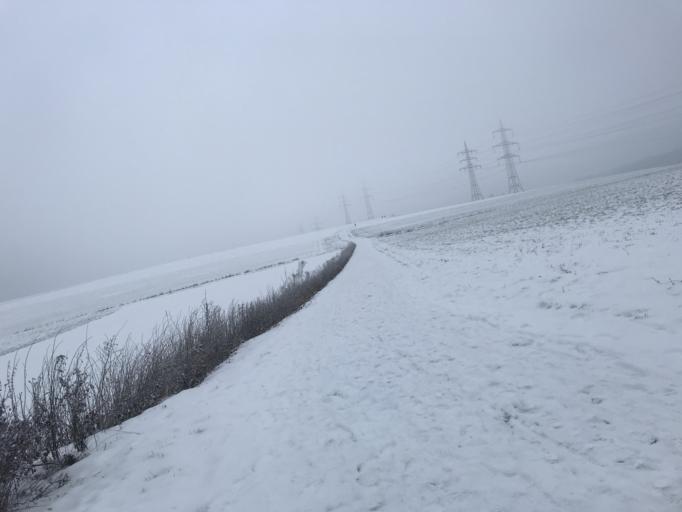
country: DE
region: Hesse
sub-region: Regierungsbezirk Darmstadt
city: Hofheim am Taunus
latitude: 50.0870
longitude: 8.4042
